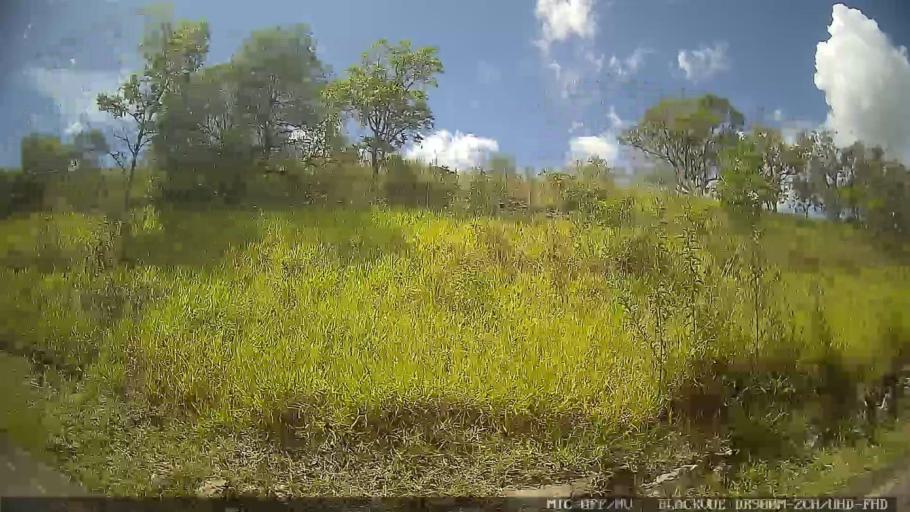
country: BR
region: Sao Paulo
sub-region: Conchas
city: Conchas
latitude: -23.0259
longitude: -48.0015
